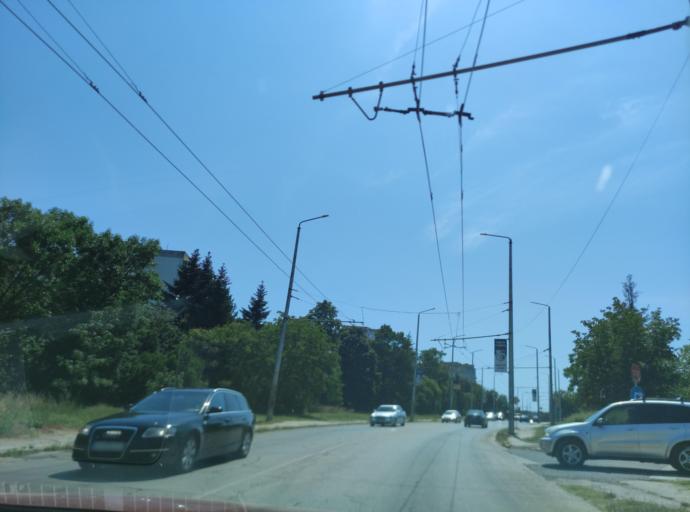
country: BG
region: Pleven
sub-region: Obshtina Pleven
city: Pleven
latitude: 43.4265
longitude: 24.5892
